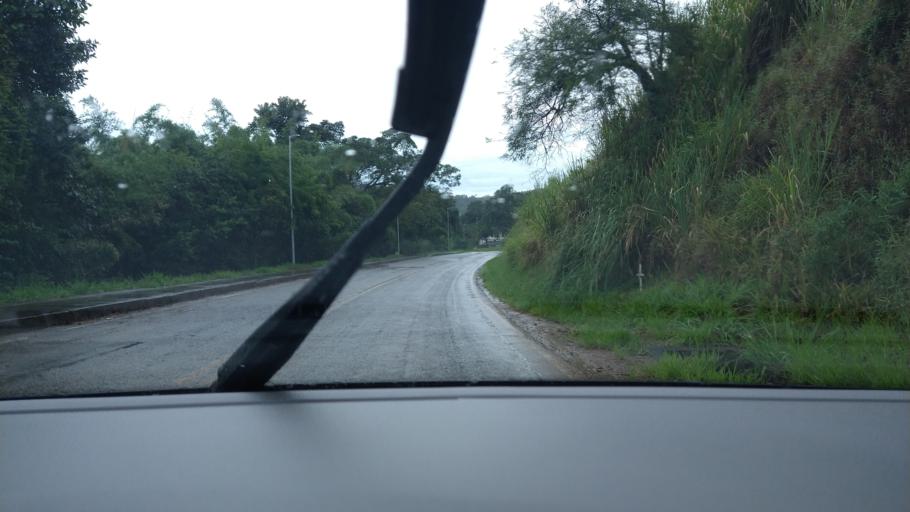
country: BR
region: Minas Gerais
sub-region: Ponte Nova
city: Ponte Nova
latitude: -20.3854
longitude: -42.9018
